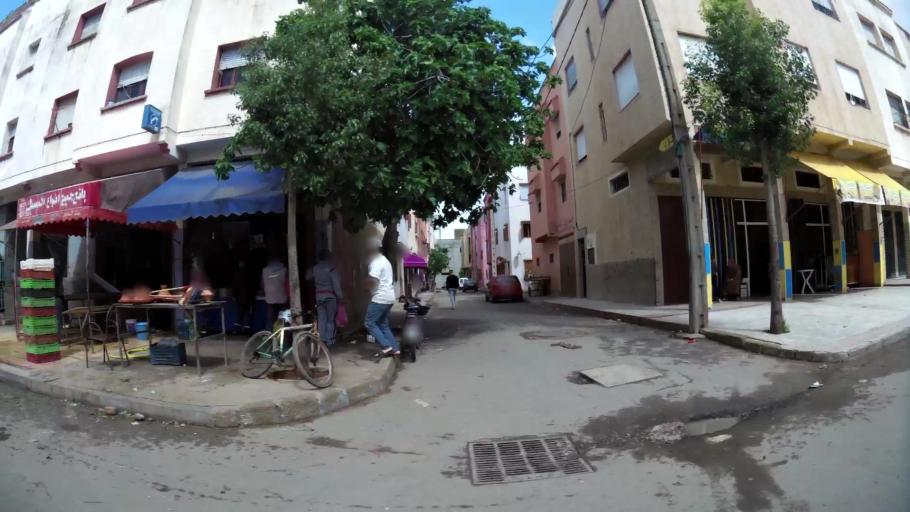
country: MA
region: Grand Casablanca
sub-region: Mediouna
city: Mediouna
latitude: 33.3675
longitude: -7.5291
